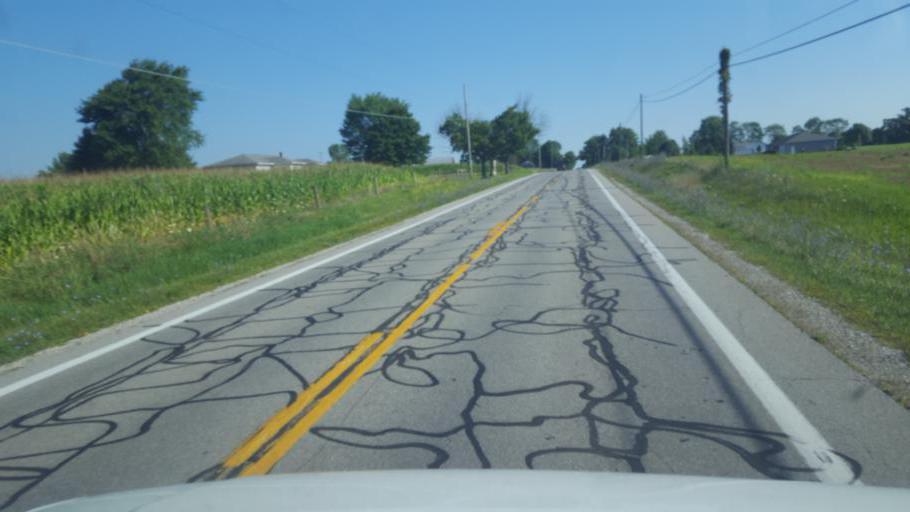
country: US
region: Ohio
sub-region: Morrow County
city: Mount Gilead
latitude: 40.5844
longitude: -82.8241
